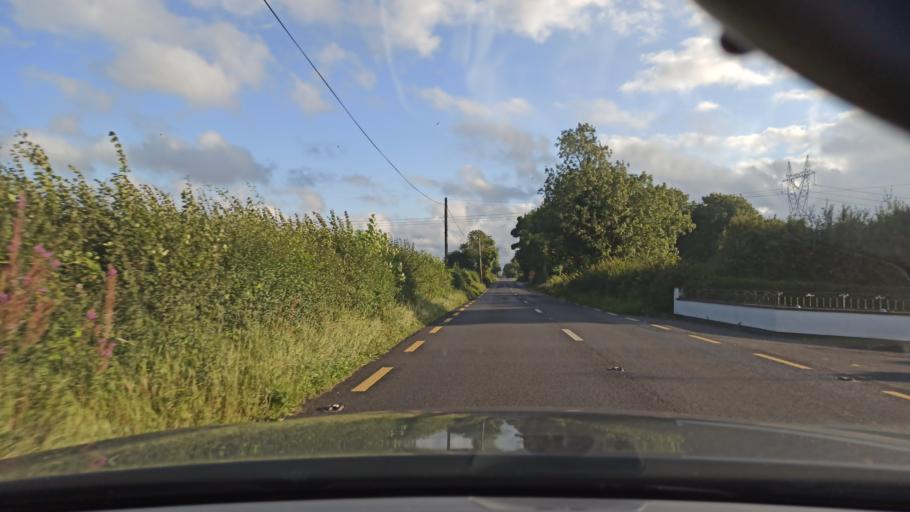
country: IE
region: Munster
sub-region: North Tipperary
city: Roscrea
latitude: 52.8967
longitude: -7.7994
